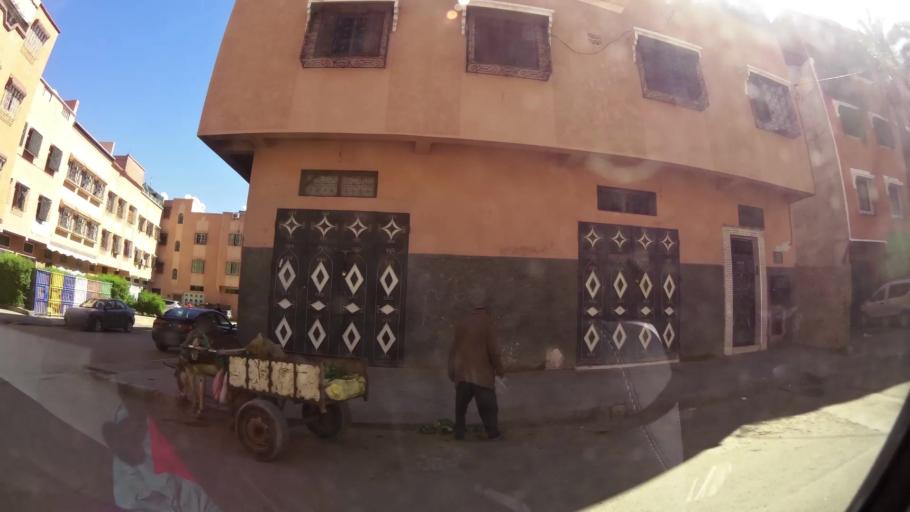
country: MA
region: Marrakech-Tensift-Al Haouz
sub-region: Marrakech
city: Marrakesh
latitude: 31.6482
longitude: -7.9809
